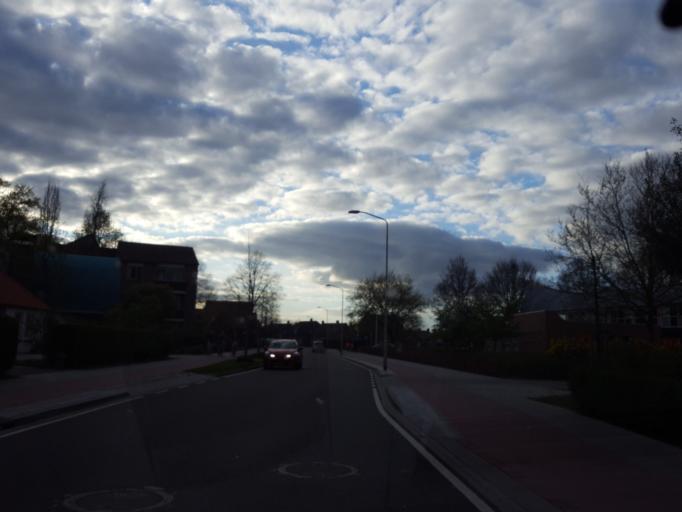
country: NL
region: North Brabant
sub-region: Gemeente Asten
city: Asten
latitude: 51.4615
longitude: 5.8060
